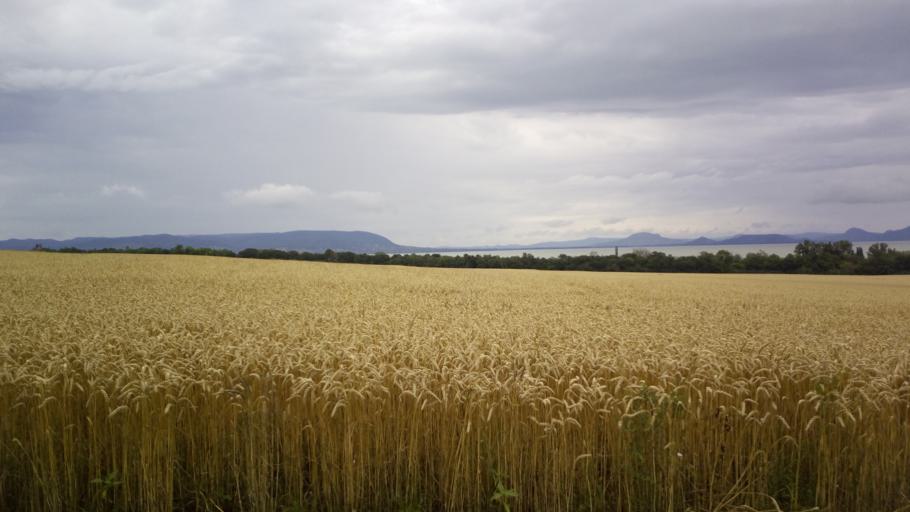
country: HU
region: Somogy
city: Balatonbereny
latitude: 46.7012
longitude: 17.3555
